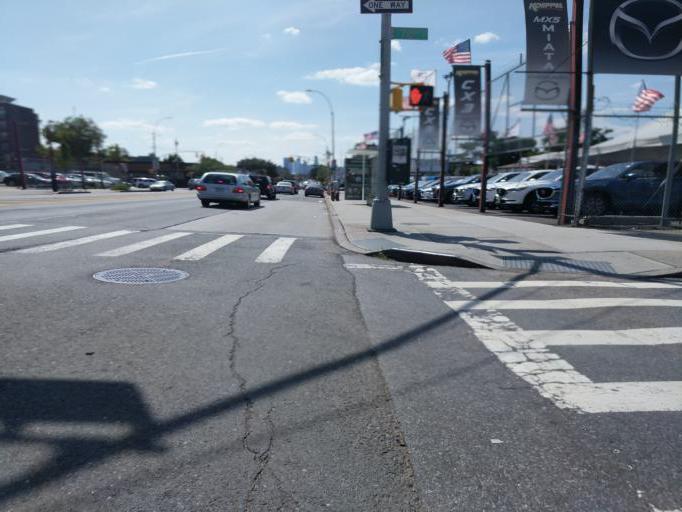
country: US
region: New York
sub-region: Queens County
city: Long Island City
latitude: 40.7553
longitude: -73.8891
